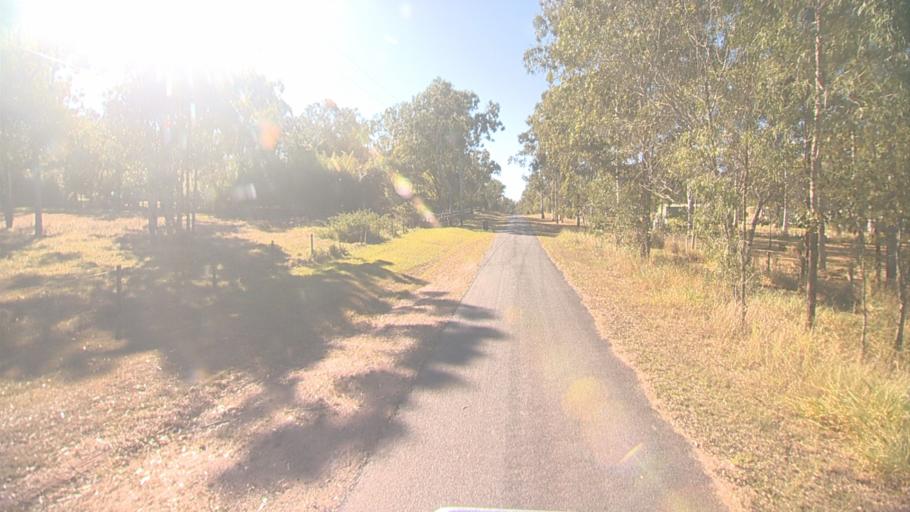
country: AU
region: Queensland
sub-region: Logan
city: Park Ridge South
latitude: -27.7287
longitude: 152.9900
